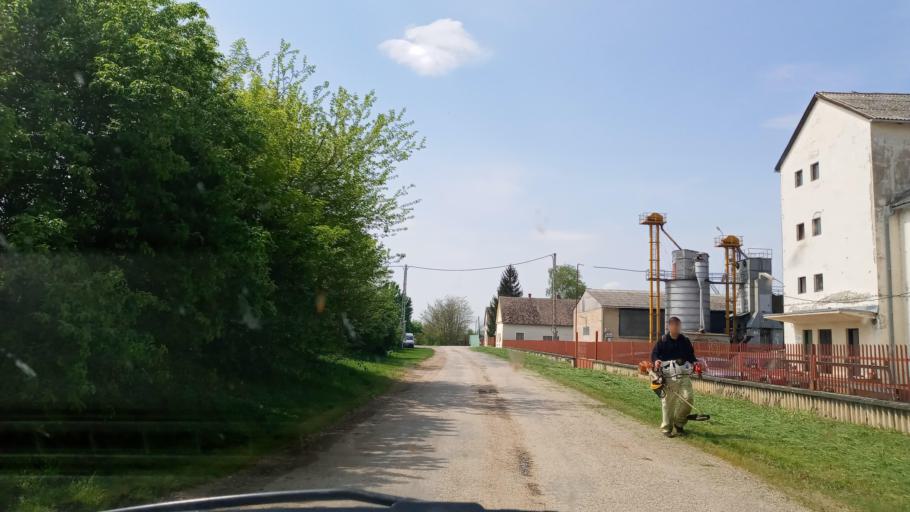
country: HU
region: Baranya
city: Boly
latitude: 45.9386
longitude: 18.5389
